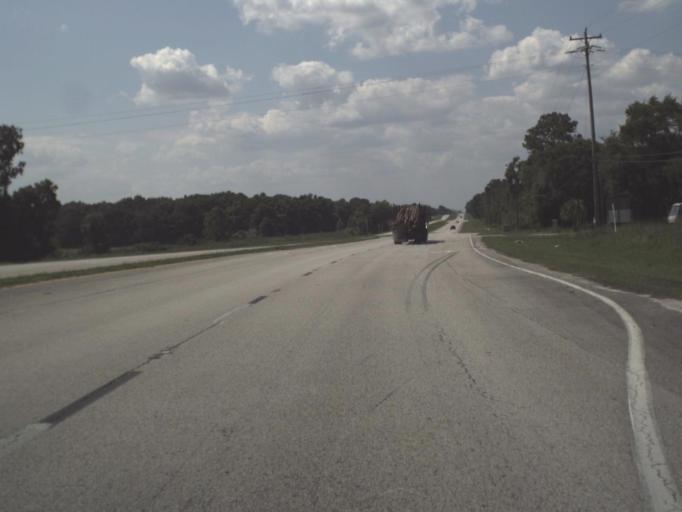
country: US
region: Florida
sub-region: Alachua County
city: Hawthorne
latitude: 29.6145
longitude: -82.0943
